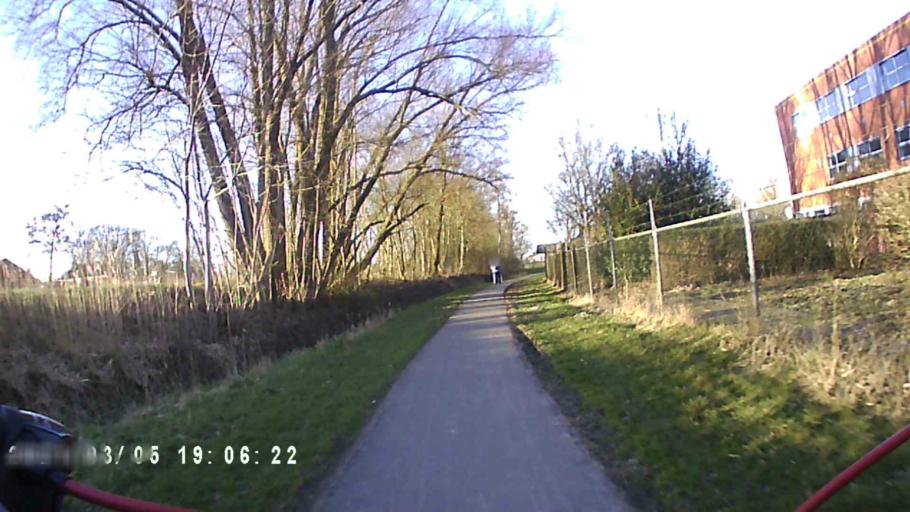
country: NL
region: Groningen
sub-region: Gemeente Winsum
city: Winsum
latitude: 53.3278
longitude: 6.5212
